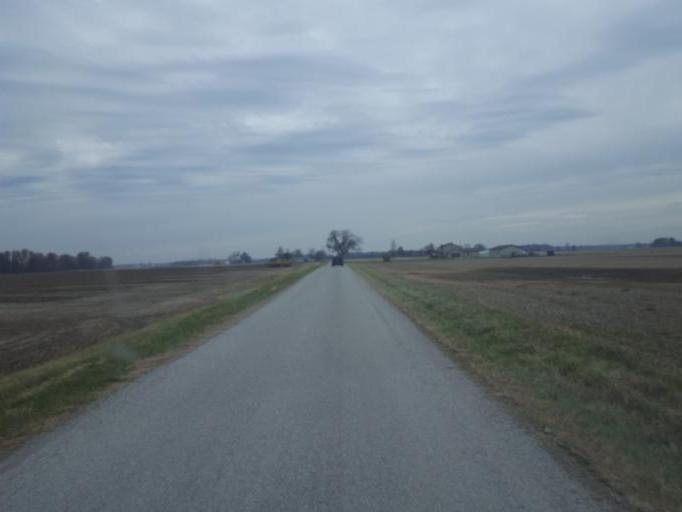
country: US
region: Ohio
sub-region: Marion County
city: Prospect
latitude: 40.4422
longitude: -83.1132
